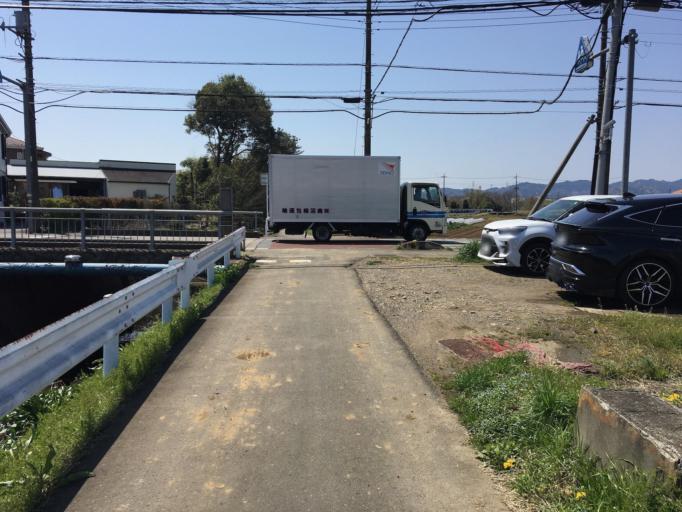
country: JP
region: Saitama
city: Sakado
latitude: 35.9458
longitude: 139.3494
